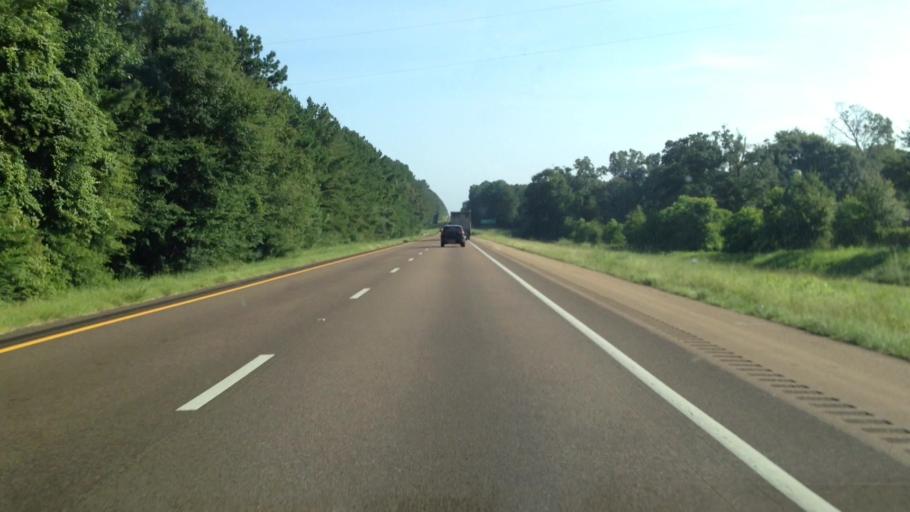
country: US
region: Mississippi
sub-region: Pike County
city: Summit
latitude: 31.2991
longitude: -90.4781
